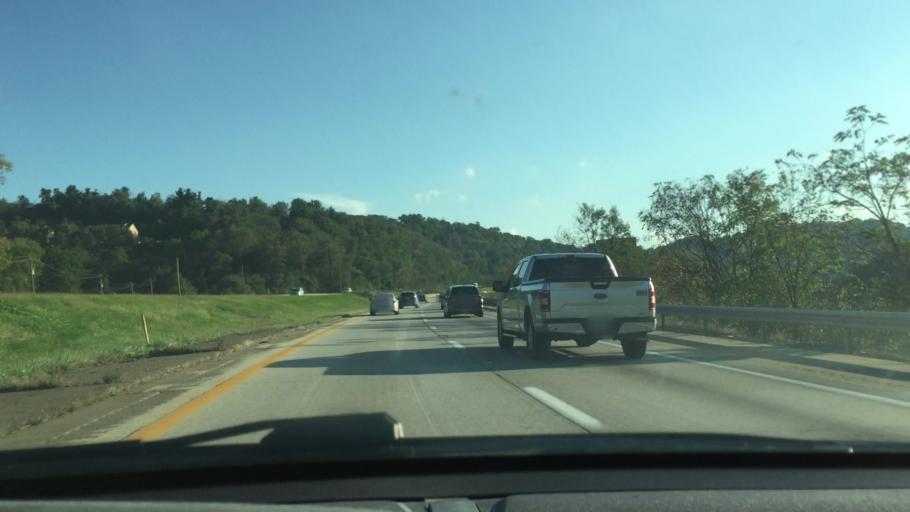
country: US
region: Pennsylvania
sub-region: Washington County
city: Canonsburg
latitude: 40.2758
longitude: -80.1586
